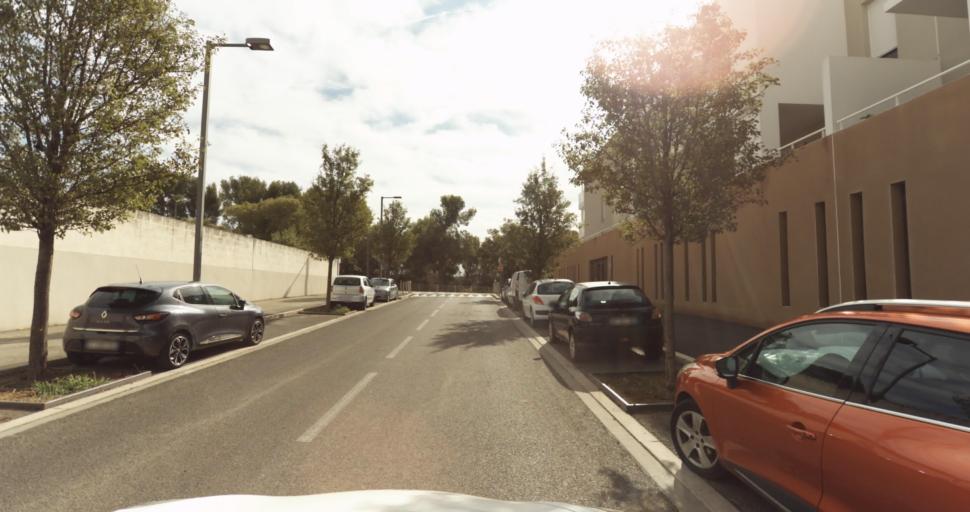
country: FR
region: Provence-Alpes-Cote d'Azur
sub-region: Departement des Bouches-du-Rhone
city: Miramas
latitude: 43.5970
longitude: 5.0105
